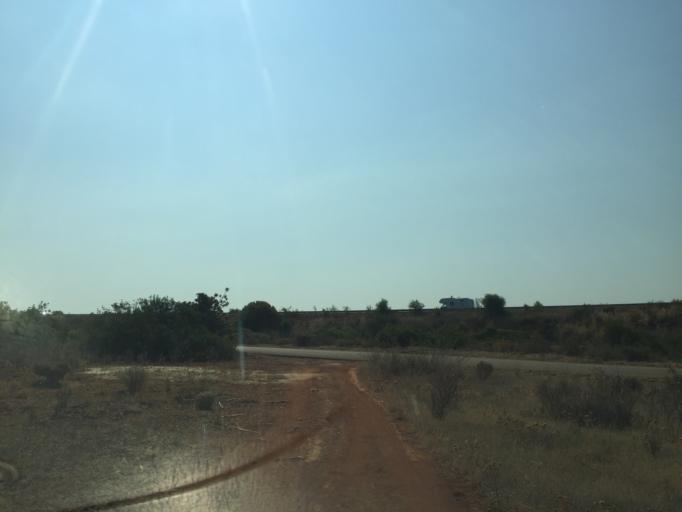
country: PT
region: Faro
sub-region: Loule
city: Almancil
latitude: 37.0923
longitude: -8.0056
